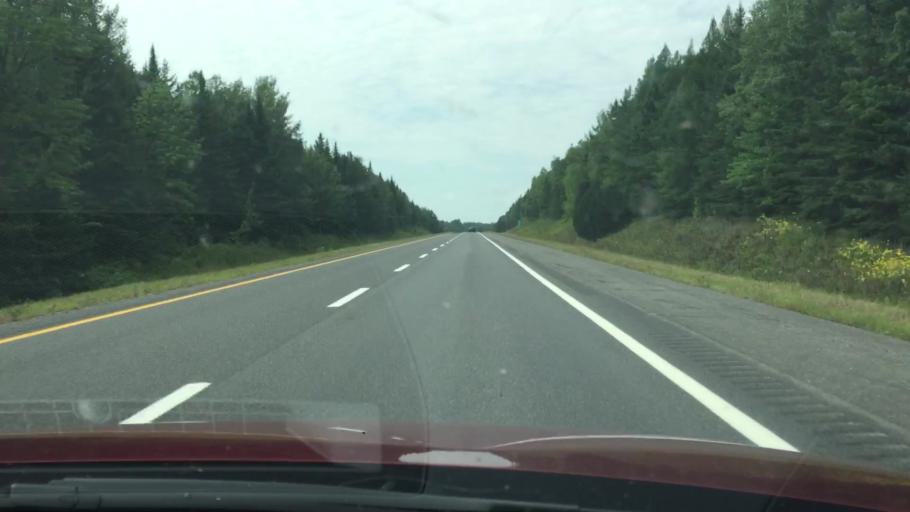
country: US
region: Maine
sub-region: Aroostook County
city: Hodgdon
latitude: 46.1408
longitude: -68.0002
